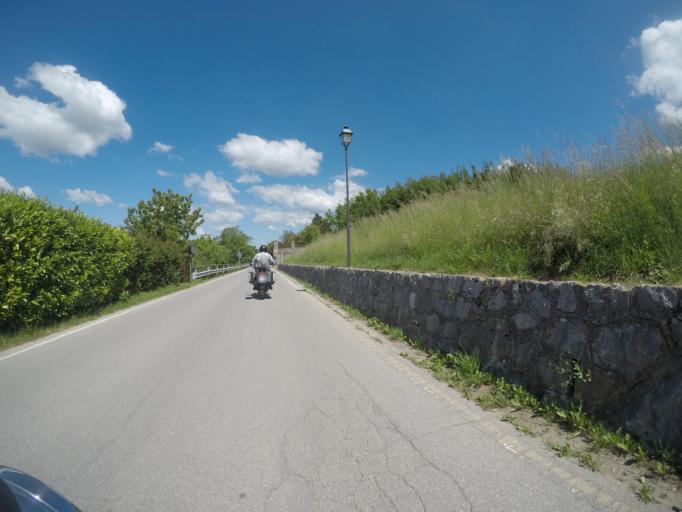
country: IT
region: Tuscany
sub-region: Provincia di Lucca
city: Careggine
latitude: 44.1187
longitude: 10.3278
